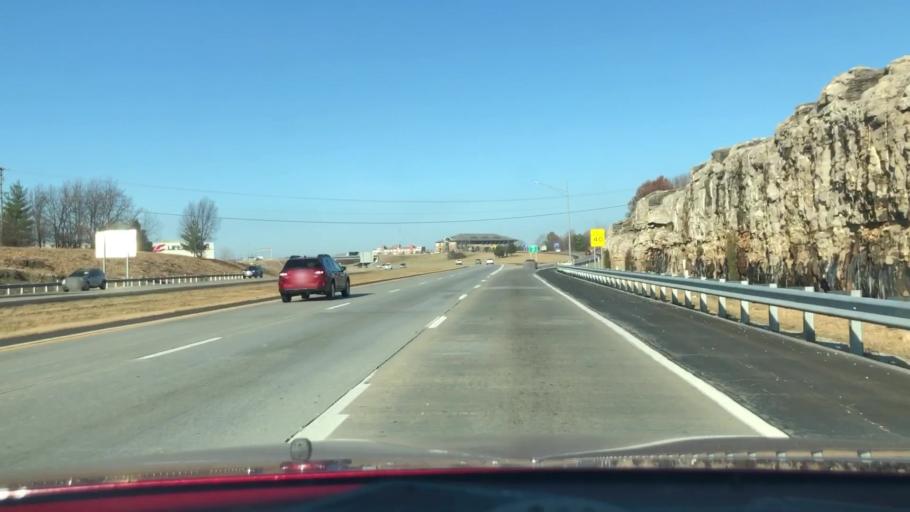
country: US
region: Missouri
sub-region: Greene County
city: Battlefield
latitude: 37.1401
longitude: -93.3133
